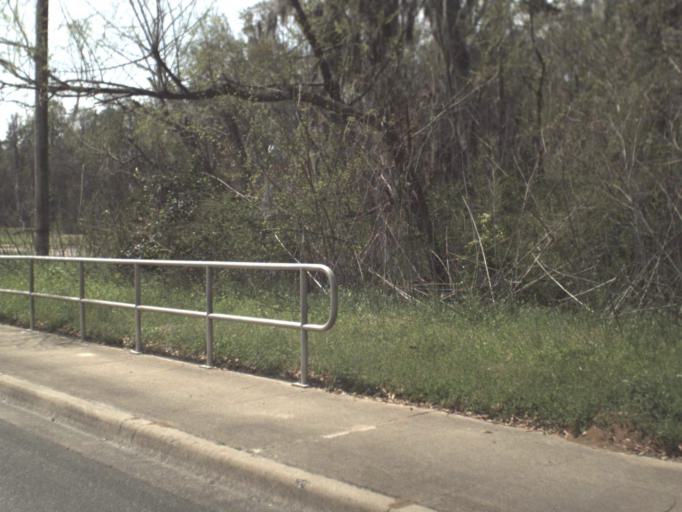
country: US
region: Florida
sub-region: Leon County
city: Tallahassee
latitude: 30.4376
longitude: -84.2268
